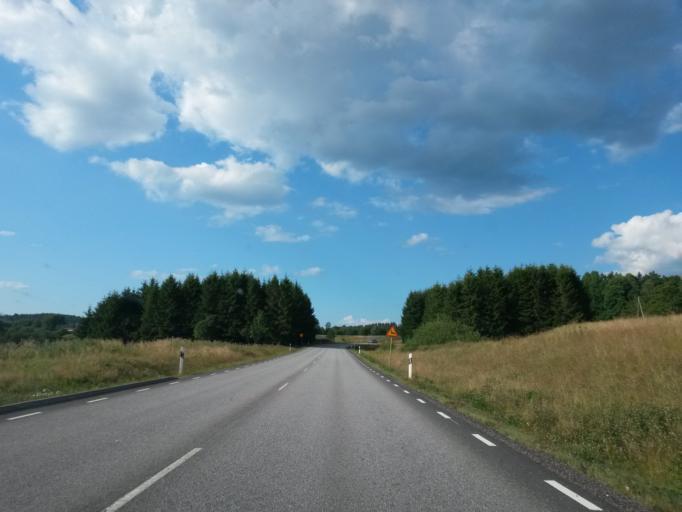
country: SE
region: Vaestra Goetaland
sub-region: Lerums Kommun
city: Stenkullen
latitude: 57.7938
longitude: 12.3024
